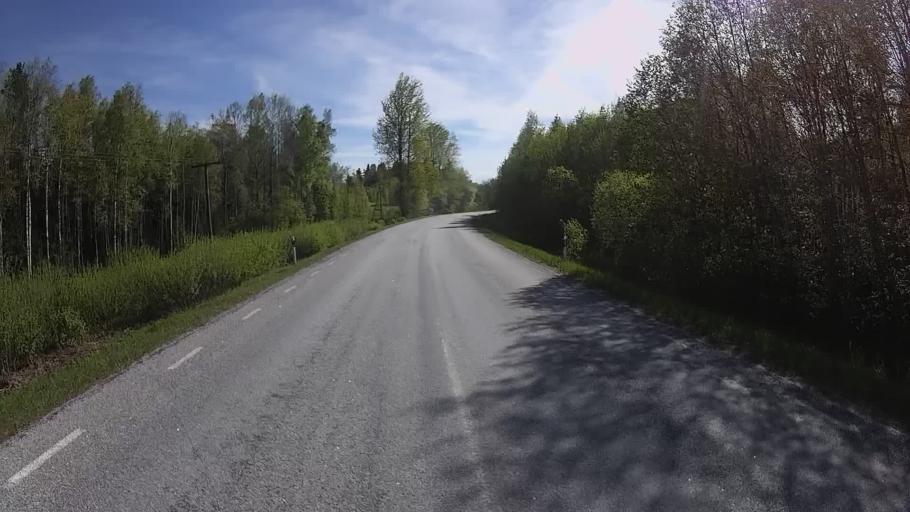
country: EE
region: Vorumaa
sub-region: Antsla vald
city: Vana-Antsla
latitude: 57.9942
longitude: 26.4938
